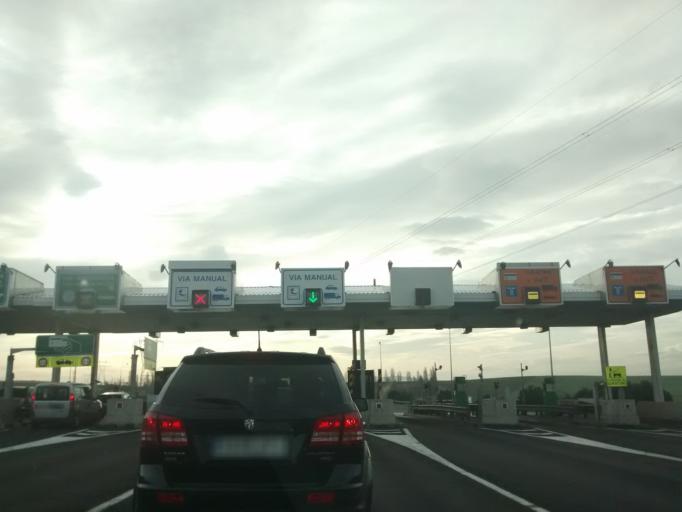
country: ES
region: Navarre
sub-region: Provincia de Navarra
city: Oltza
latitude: 42.8679
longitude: -1.7489
